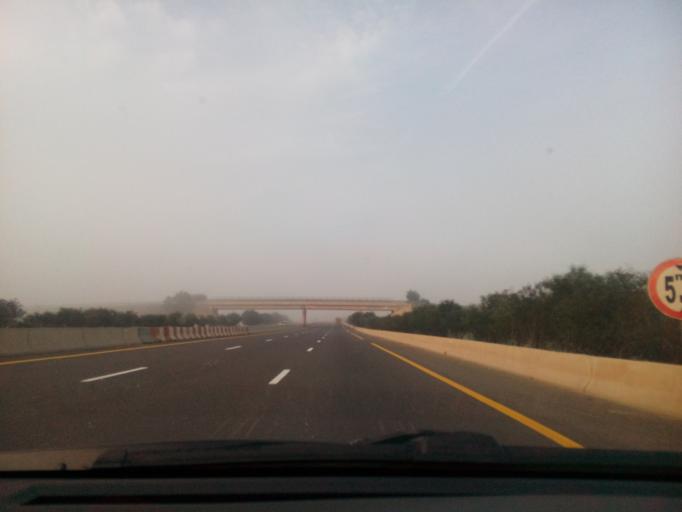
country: DZ
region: Relizane
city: Relizane
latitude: 35.7949
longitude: 0.4931
